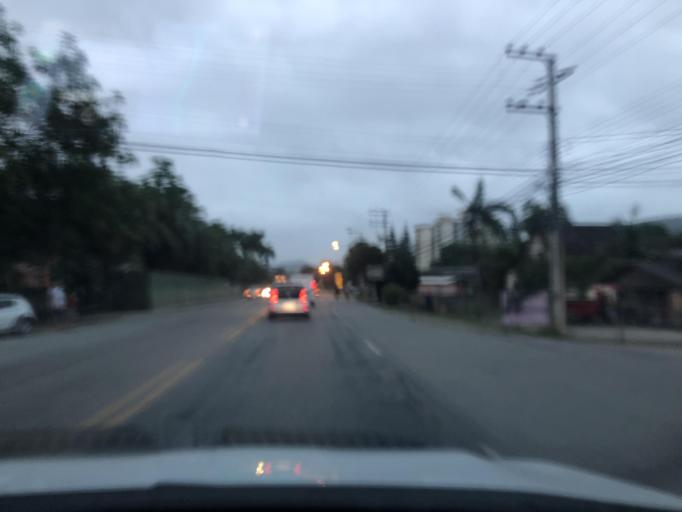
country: BR
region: Santa Catarina
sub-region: Pomerode
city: Pomerode
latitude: -26.7918
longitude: -49.0869
